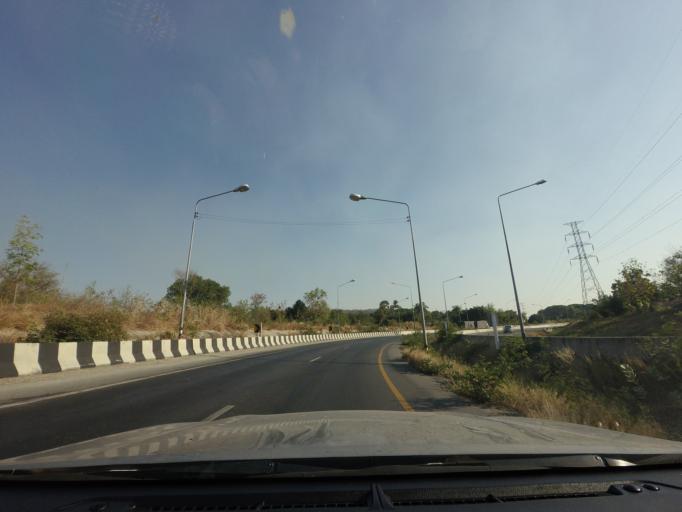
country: TH
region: Nakhon Sawan
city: Krok Phra
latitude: 15.6150
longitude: 100.1225
